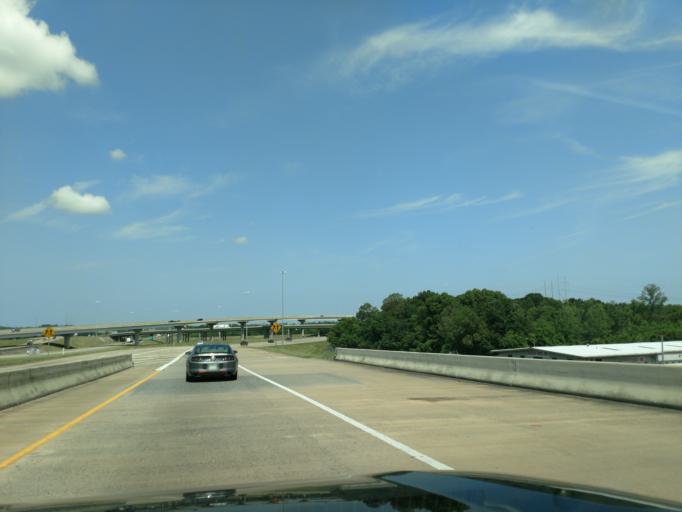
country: US
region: Mississippi
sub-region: Hinds County
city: Jackson
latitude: 32.2760
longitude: -90.1692
